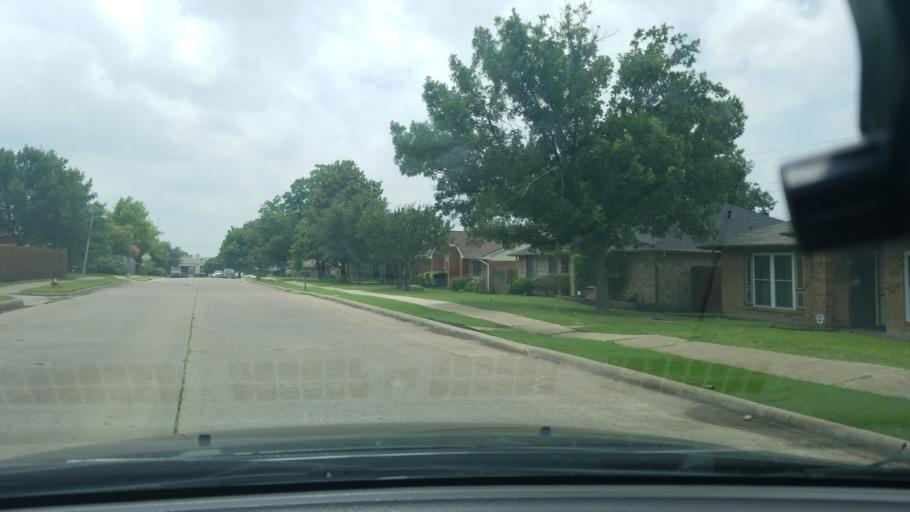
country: US
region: Texas
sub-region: Dallas County
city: Mesquite
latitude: 32.8031
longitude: -96.6216
